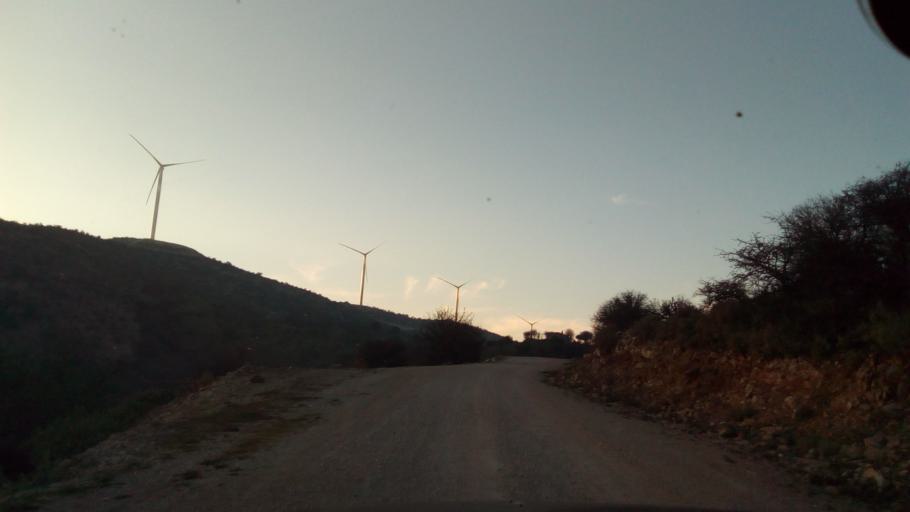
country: GR
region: West Greece
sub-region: Nomos Aitolias kai Akarnanias
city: Nafpaktos
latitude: 38.4579
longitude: 21.8399
